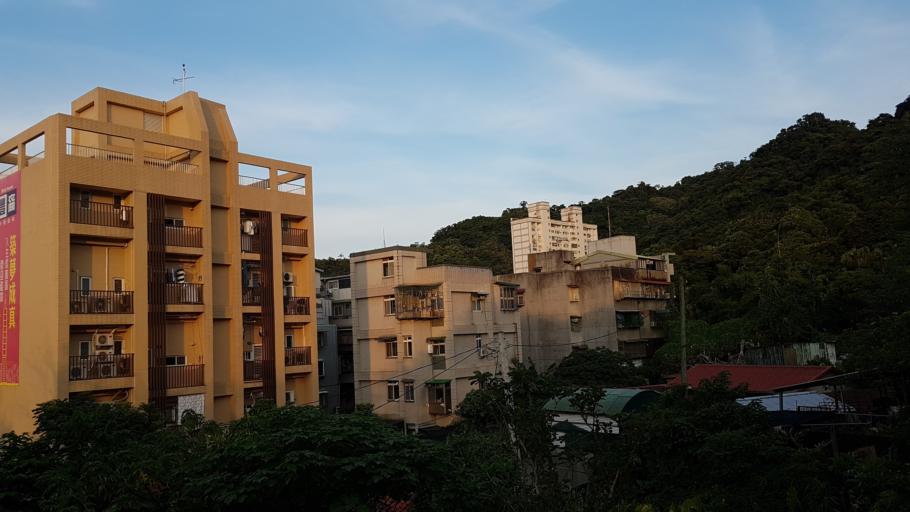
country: TW
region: Taipei
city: Taipei
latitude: 25.0230
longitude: 121.5604
